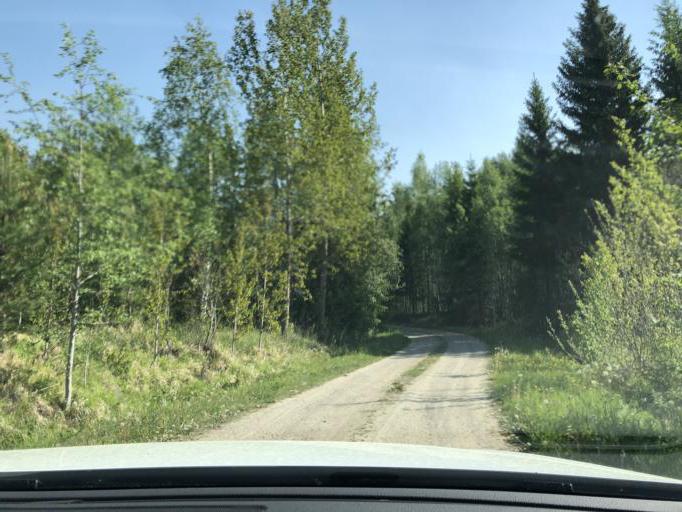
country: SE
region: Dalarna
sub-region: Avesta Kommun
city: Horndal
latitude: 60.2130
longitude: 16.4925
